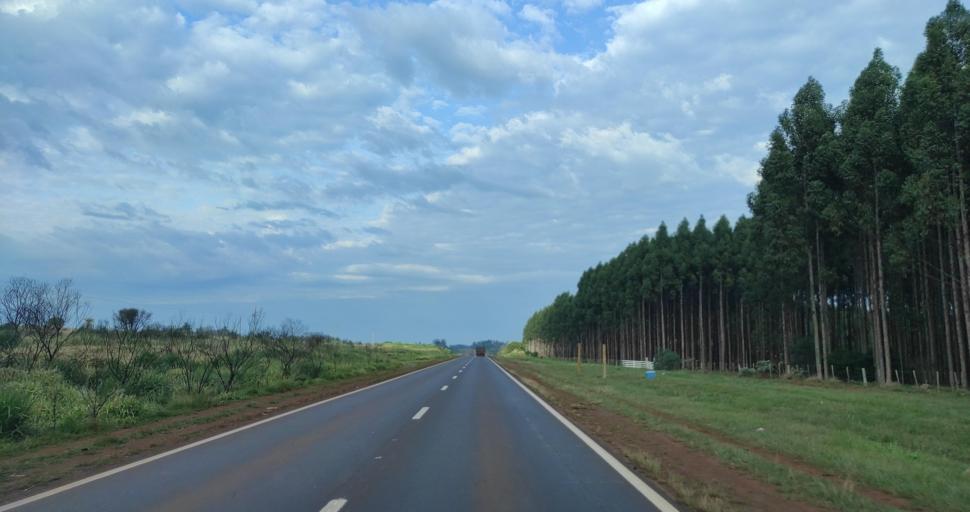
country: AR
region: Corrientes
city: San Carlos
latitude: -27.8579
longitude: -55.9212
